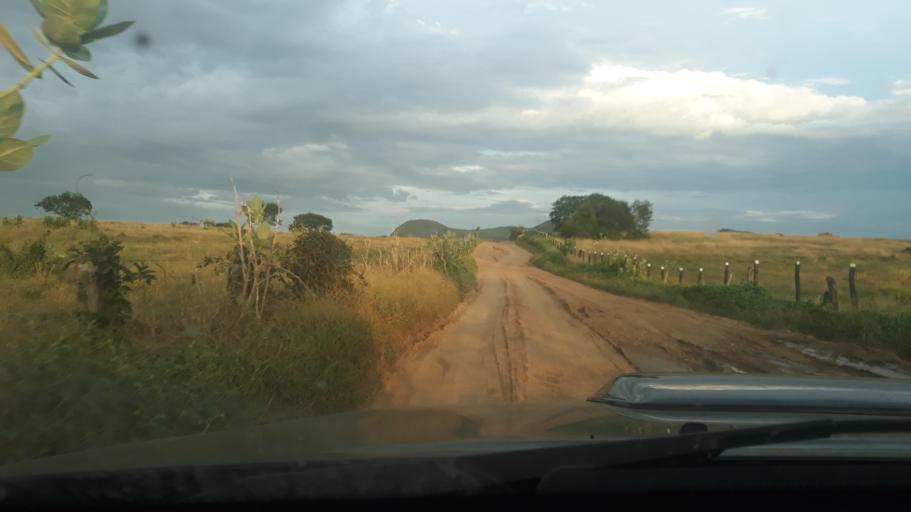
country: BR
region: Bahia
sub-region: Riacho De Santana
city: Riacho de Santana
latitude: -13.9005
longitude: -42.8677
